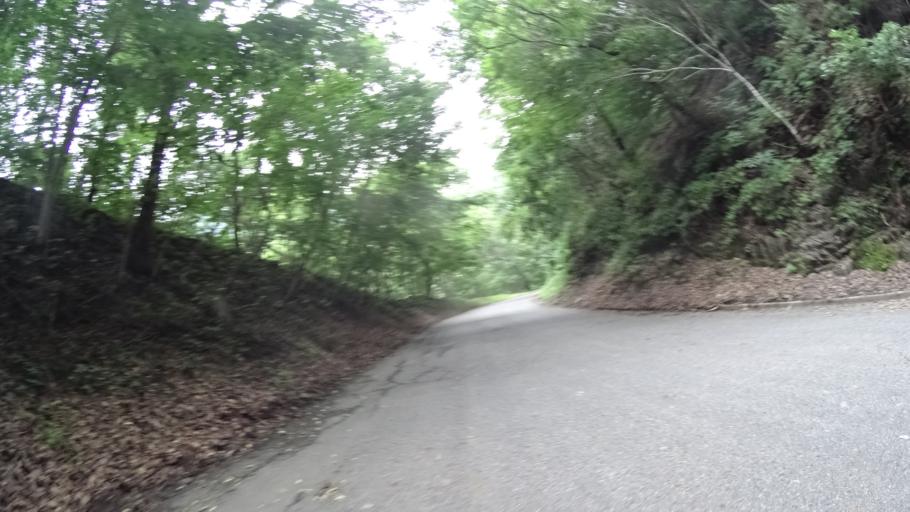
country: JP
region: Nagano
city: Saku
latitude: 36.0919
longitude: 138.6874
